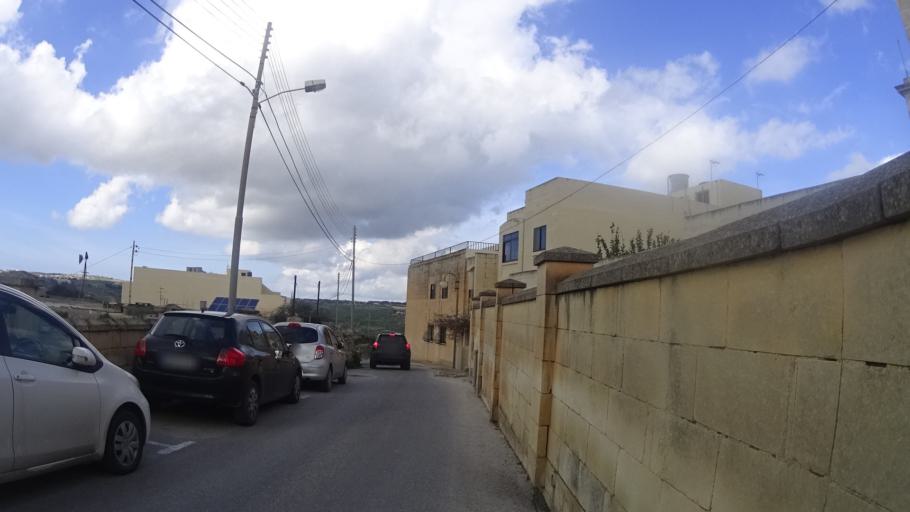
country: MT
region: L-Imtarfa
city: Imtarfa
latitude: 35.8910
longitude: 14.3973
